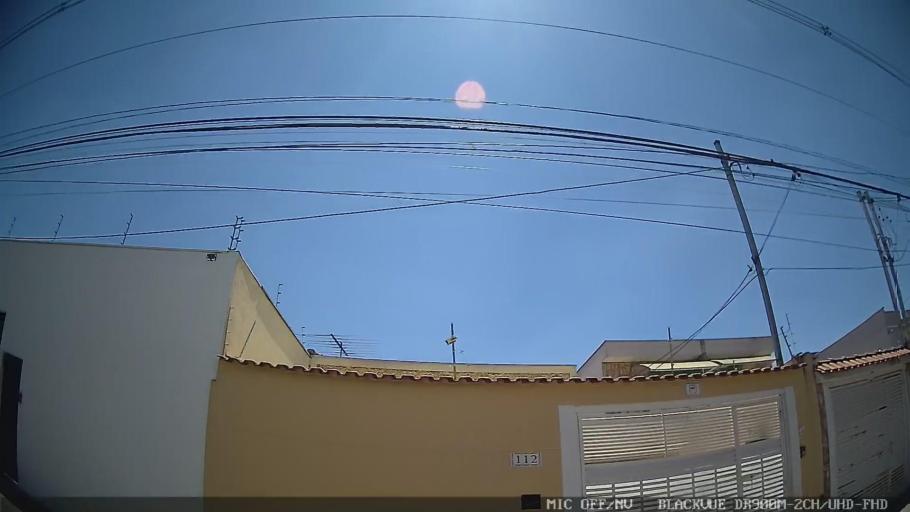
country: BR
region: Sao Paulo
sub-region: Sao Caetano Do Sul
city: Sao Caetano do Sul
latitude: -23.5887
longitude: -46.5853
